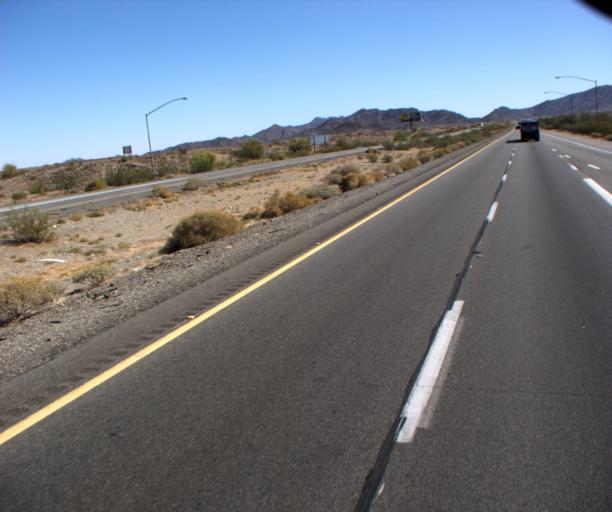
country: US
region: Arizona
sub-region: La Paz County
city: Ehrenberg
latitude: 33.6248
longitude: -114.4318
